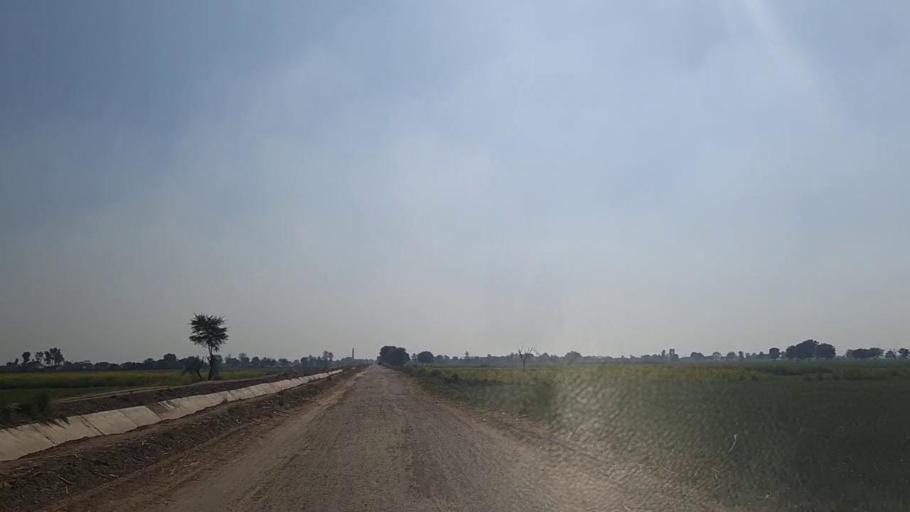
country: PK
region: Sindh
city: Shahpur Chakar
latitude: 26.1985
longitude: 68.5836
